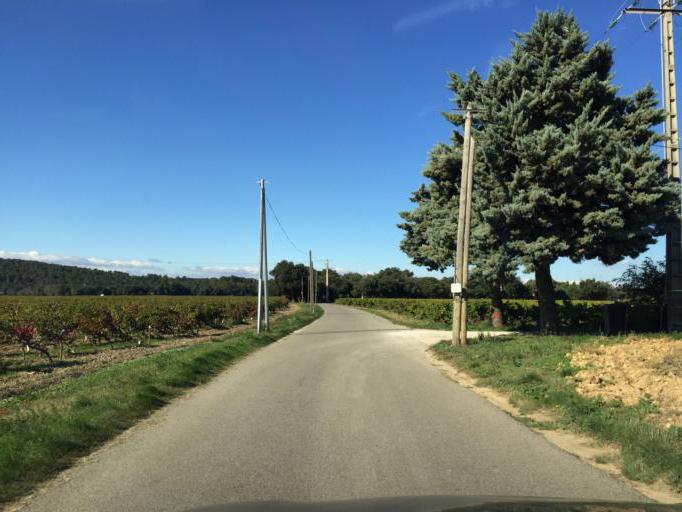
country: FR
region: Provence-Alpes-Cote d'Azur
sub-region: Departement du Vaucluse
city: Orange
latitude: 44.1645
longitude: 4.7917
